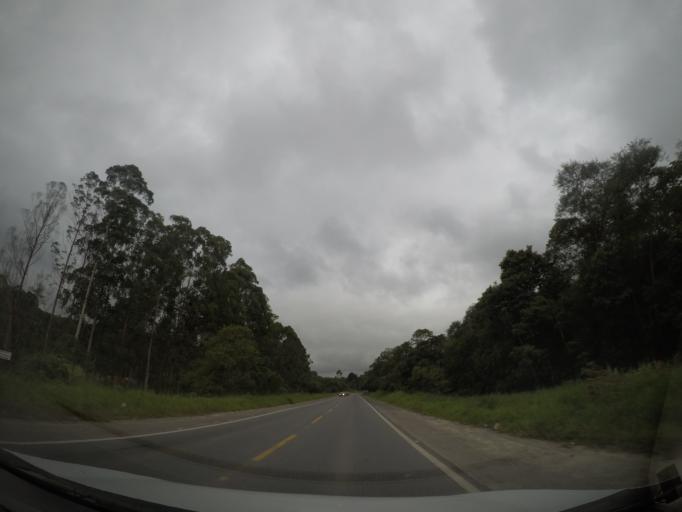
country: BR
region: Sao Paulo
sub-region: Aruja
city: Aruja
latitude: -23.3761
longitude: -46.4322
